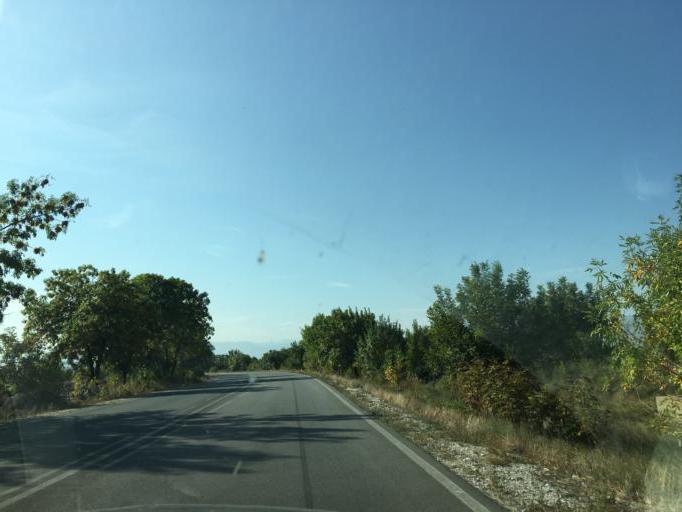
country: BG
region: Pazardzhik
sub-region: Obshtina Pazardzhik
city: Pazardzhik
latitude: 42.2255
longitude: 24.3103
